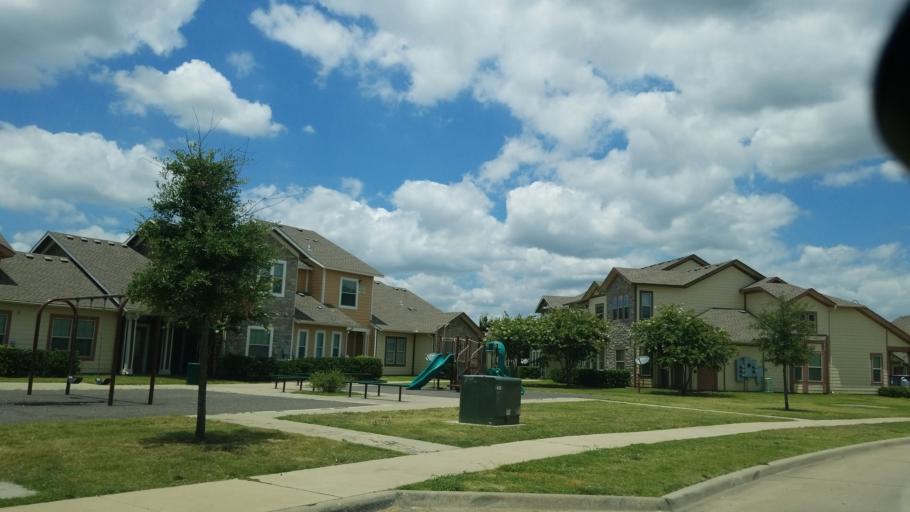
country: US
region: Texas
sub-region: Dallas County
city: Dallas
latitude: 32.7380
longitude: -96.7557
